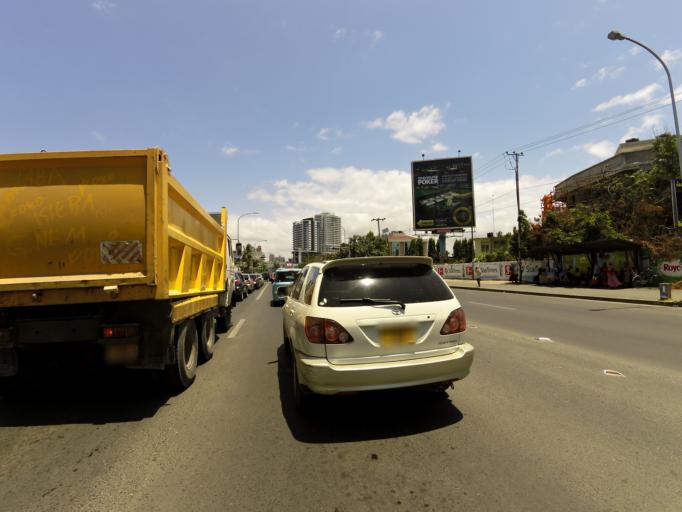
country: TZ
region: Dar es Salaam
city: Dar es Salaam
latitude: -6.8047
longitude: 39.2863
